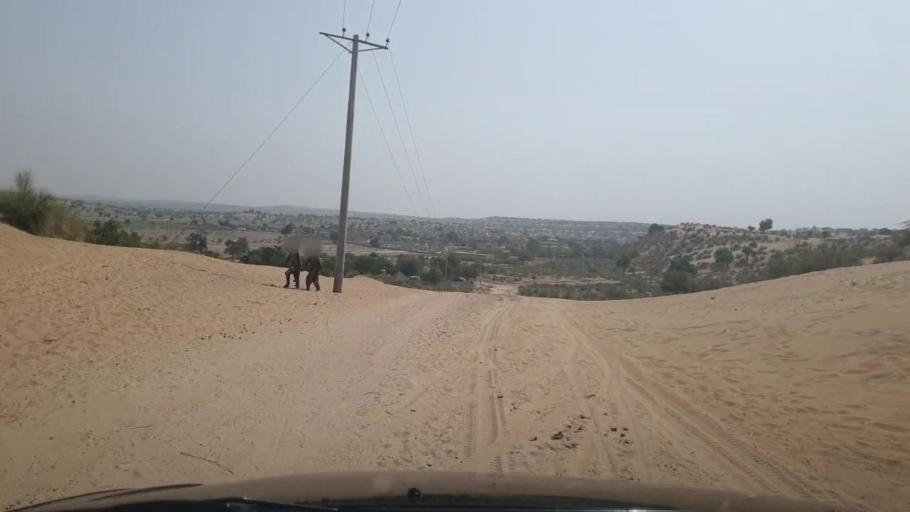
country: PK
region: Sindh
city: Islamkot
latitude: 24.9471
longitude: 70.4227
